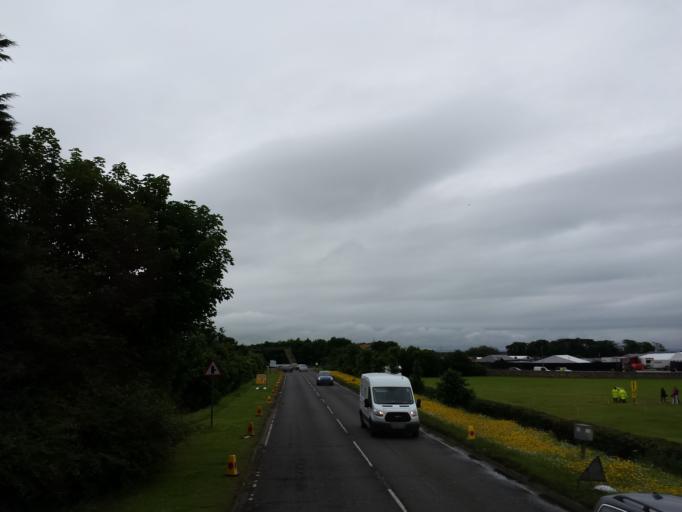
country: GB
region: Scotland
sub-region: Fife
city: Saint Andrews
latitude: 56.3444
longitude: -2.8176
